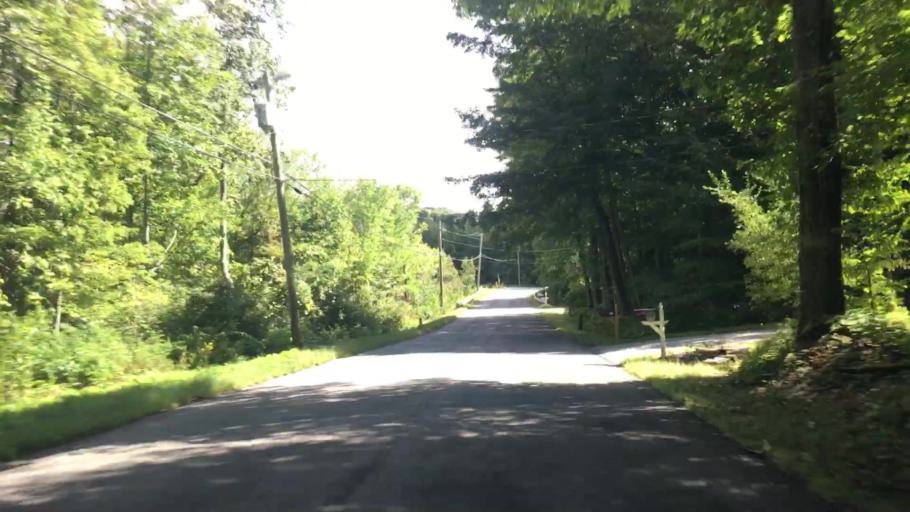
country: US
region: Connecticut
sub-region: Tolland County
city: Stafford Springs
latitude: 41.9179
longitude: -72.1968
